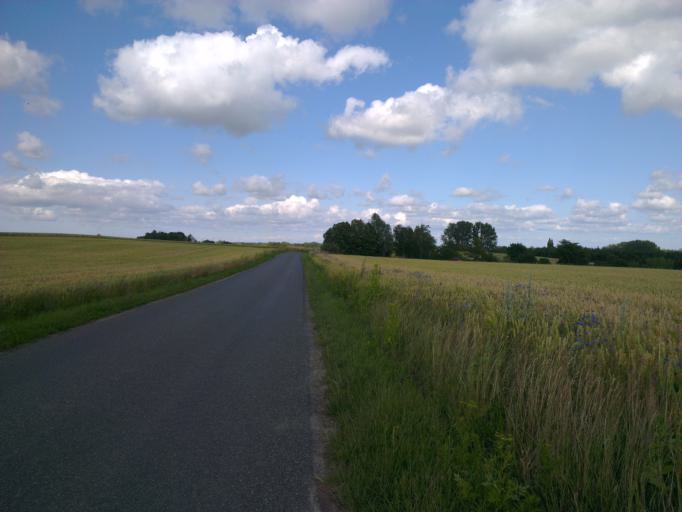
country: DK
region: Capital Region
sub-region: Frederikssund Kommune
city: Skibby
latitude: 55.7511
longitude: 12.0321
